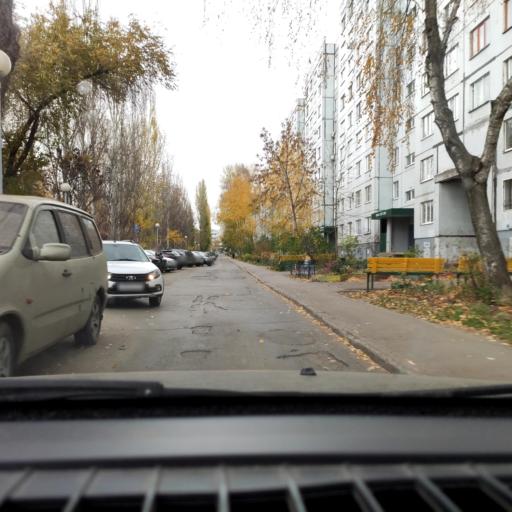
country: RU
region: Samara
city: Tol'yatti
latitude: 53.5260
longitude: 49.2848
